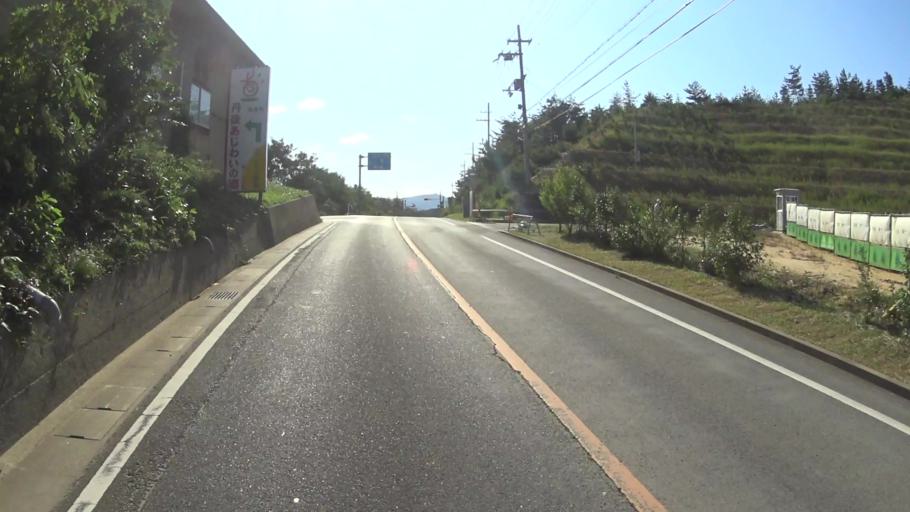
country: JP
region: Kyoto
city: Miyazu
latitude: 35.6966
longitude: 135.0528
